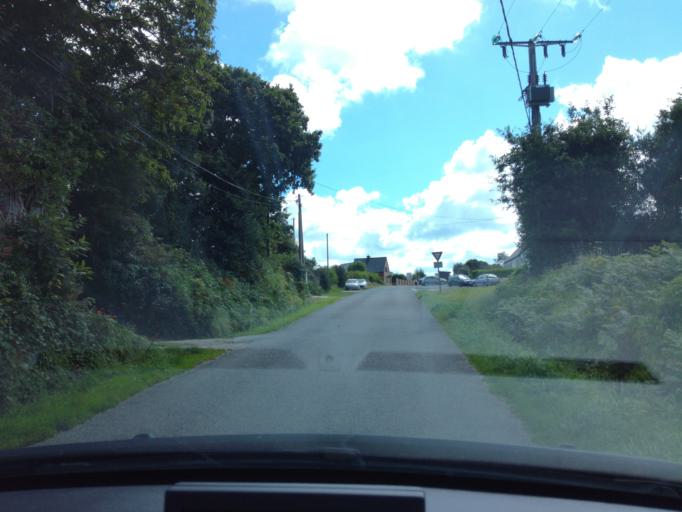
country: FR
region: Brittany
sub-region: Departement du Finistere
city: Plouguin
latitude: 48.5303
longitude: -4.5975
